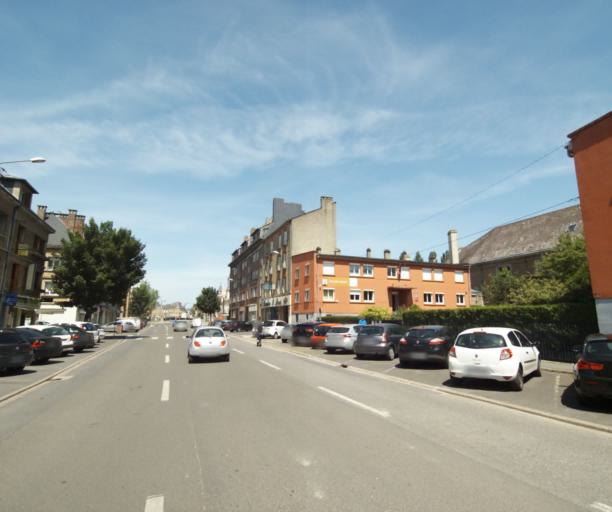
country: FR
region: Champagne-Ardenne
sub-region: Departement des Ardennes
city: Charleville-Mezieres
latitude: 49.7574
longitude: 4.7184
